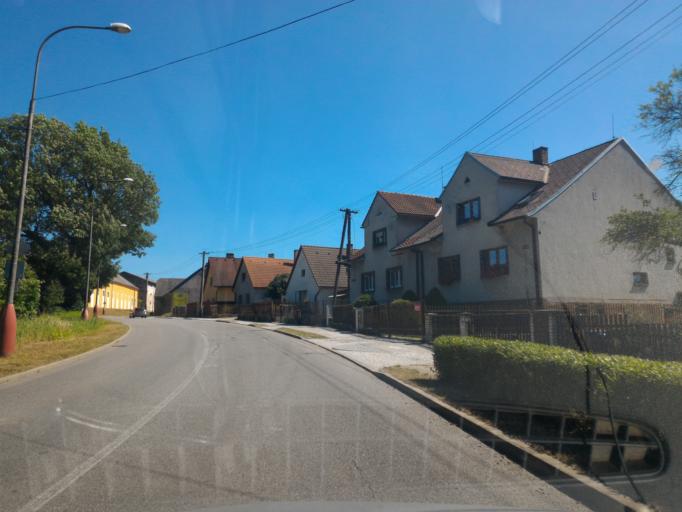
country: CZ
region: Vysocina
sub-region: Okres Jihlava
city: Trest'
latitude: 49.2979
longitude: 15.4835
